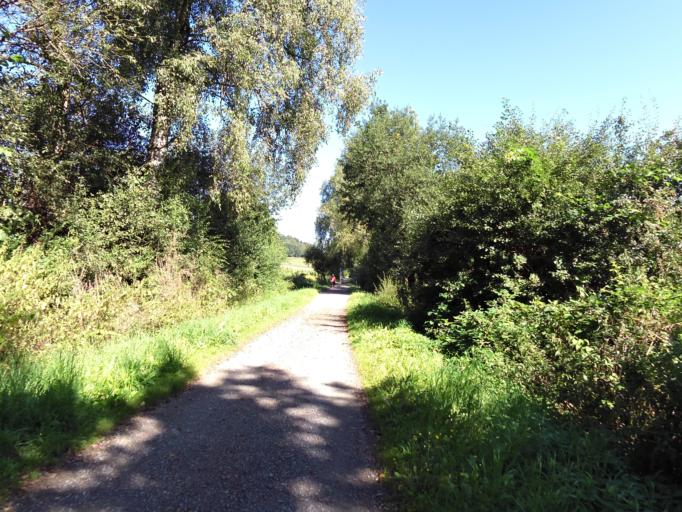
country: DE
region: Hesse
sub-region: Regierungsbezirk Darmstadt
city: Wald-Michelbach
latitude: 49.6020
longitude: 8.8519
